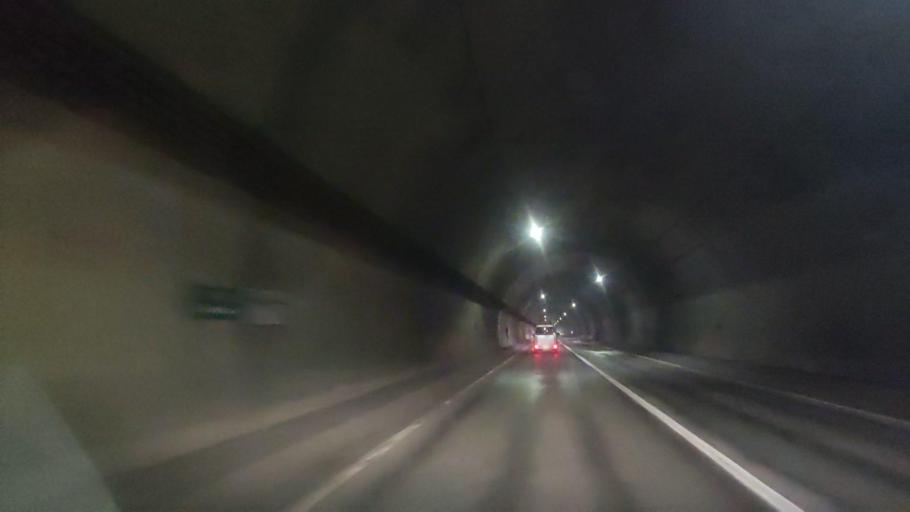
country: JP
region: Hokkaido
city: Niseko Town
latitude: 42.5958
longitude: 140.5442
